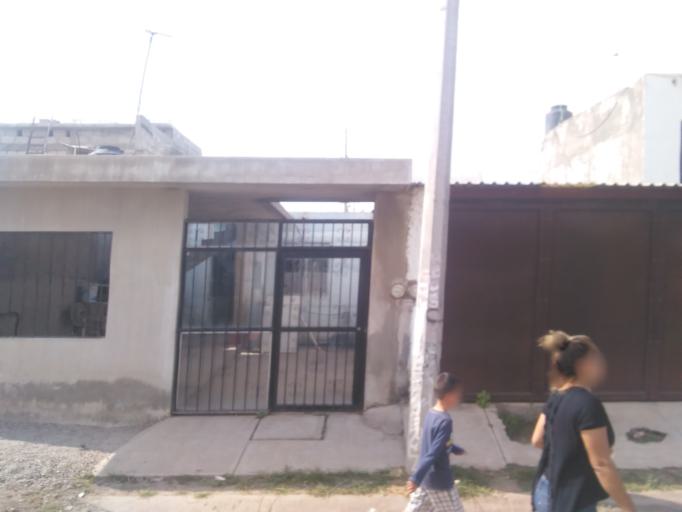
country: MX
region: Nayarit
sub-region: Tepic
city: La Corregidora
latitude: 21.4855
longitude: -104.8340
